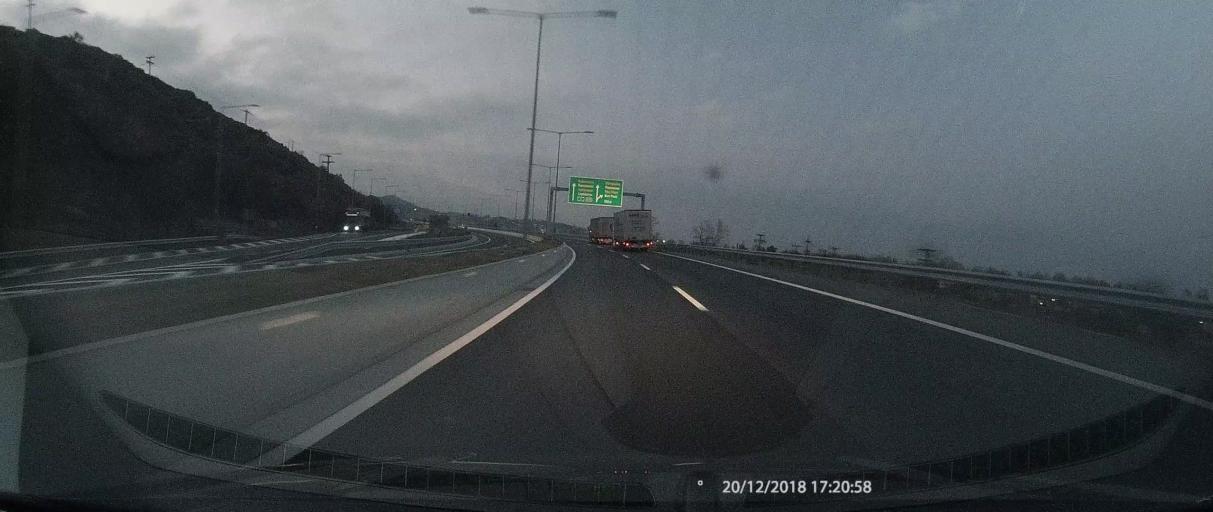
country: GR
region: Thessaly
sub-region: Nomos Larisis
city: Pyrgetos
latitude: 39.9741
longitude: 22.6376
